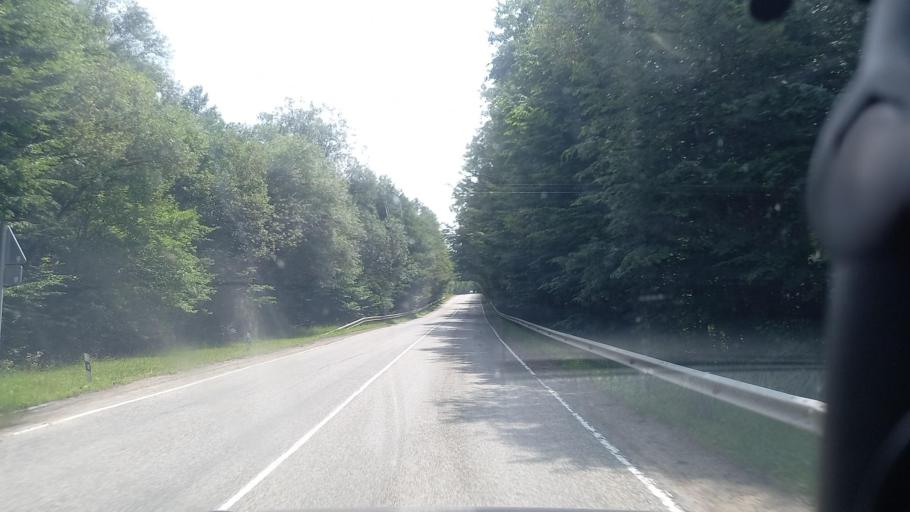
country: RU
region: Karachayevo-Cherkesiya
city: Kurdzhinovo
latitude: 44.0390
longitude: 40.9044
